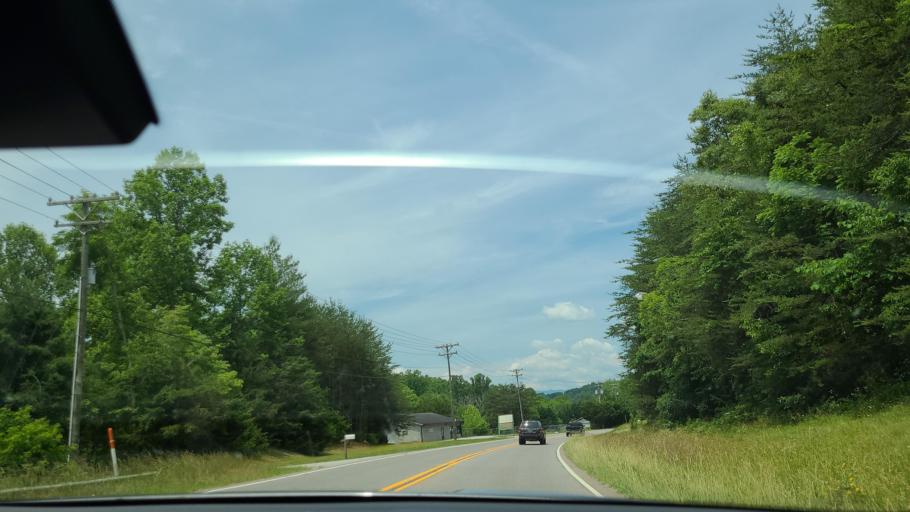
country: US
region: North Carolina
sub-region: Macon County
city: Franklin
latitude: 35.1660
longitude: -83.3328
